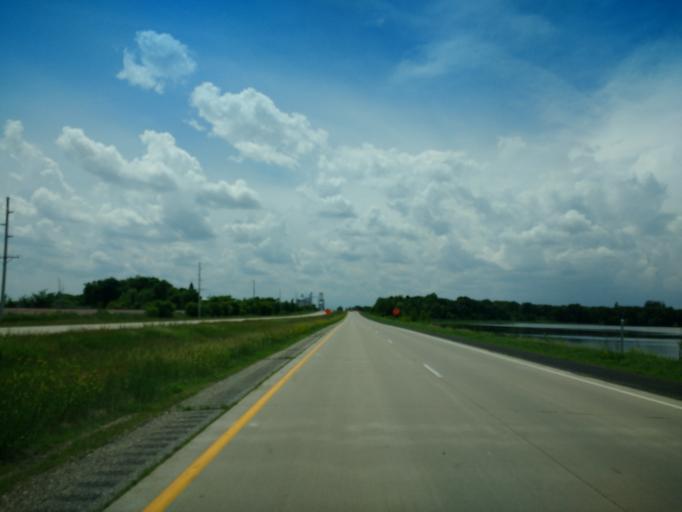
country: US
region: Minnesota
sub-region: Jackson County
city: Lakefield
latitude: 43.8056
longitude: -95.3068
